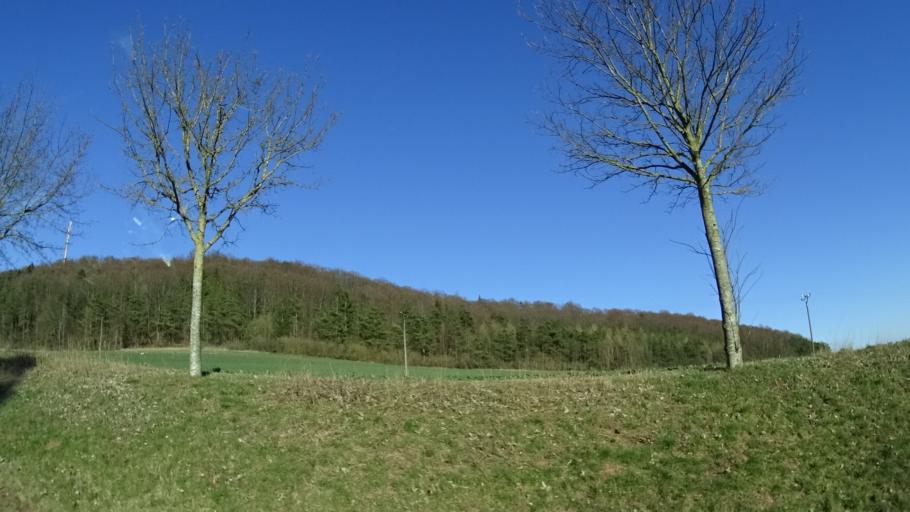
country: DE
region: Bavaria
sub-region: Regierungsbezirk Unterfranken
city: Willmars
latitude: 50.5342
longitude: 10.2824
